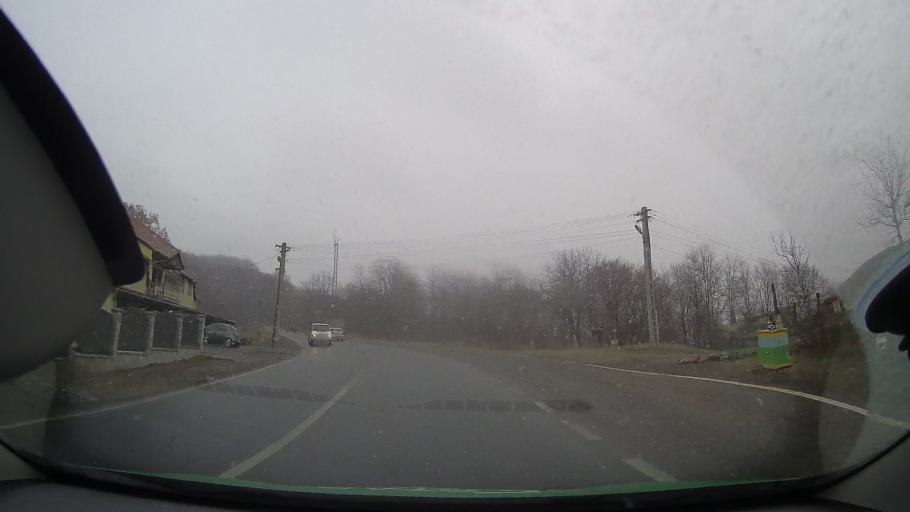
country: RO
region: Sibiu
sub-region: Municipiul Medias
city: Medias
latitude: 46.1840
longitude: 24.3257
